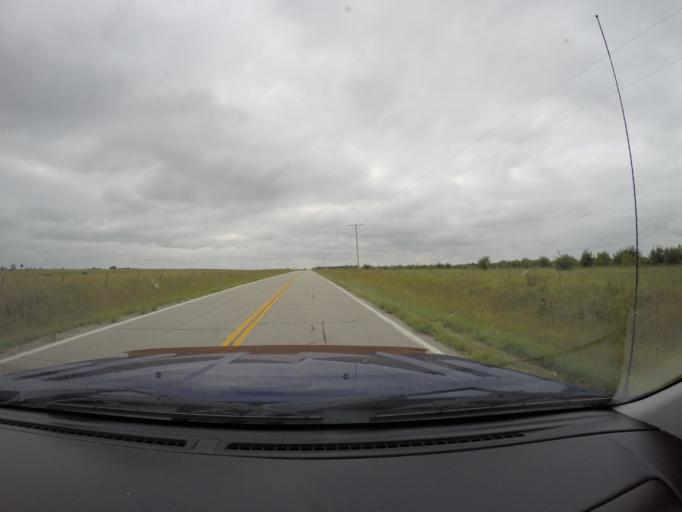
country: US
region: Kansas
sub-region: Morris County
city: Council Grove
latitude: 38.7977
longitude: -96.6374
